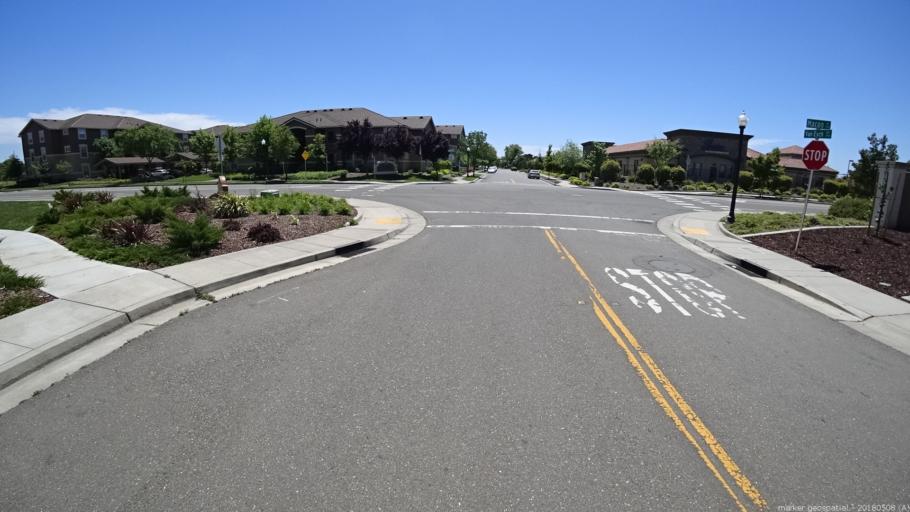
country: US
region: California
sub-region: Sacramento County
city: Elverta
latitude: 38.6802
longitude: -121.5299
